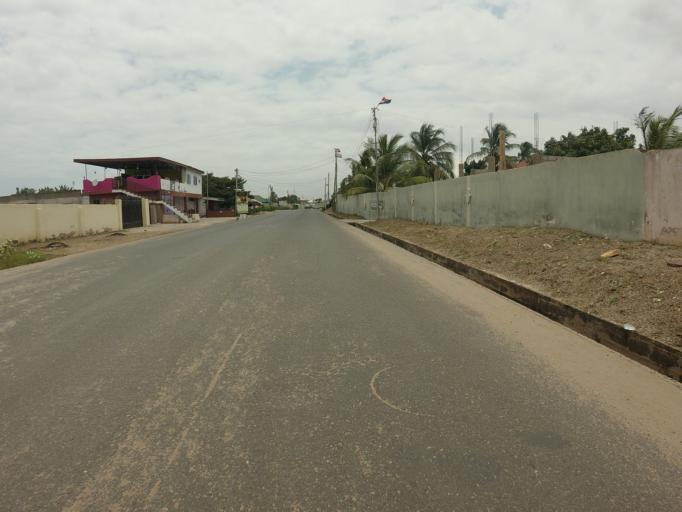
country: GH
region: Greater Accra
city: Nungua
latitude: 5.6179
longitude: -0.0829
